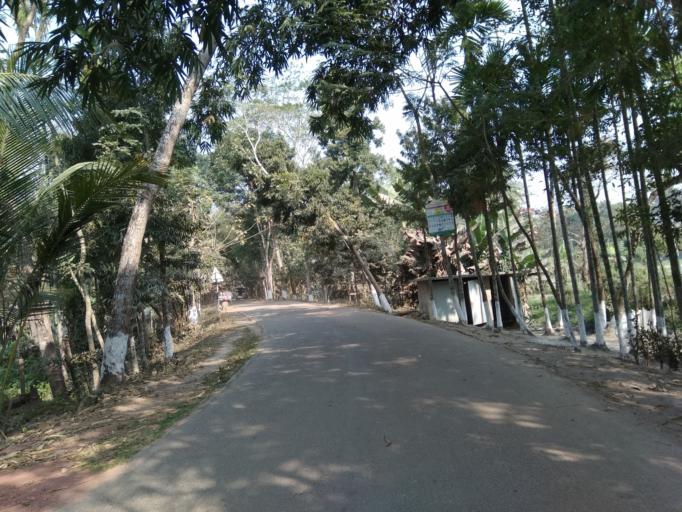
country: BD
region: Barisal
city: Mehendiganj
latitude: 22.9542
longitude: 90.4154
